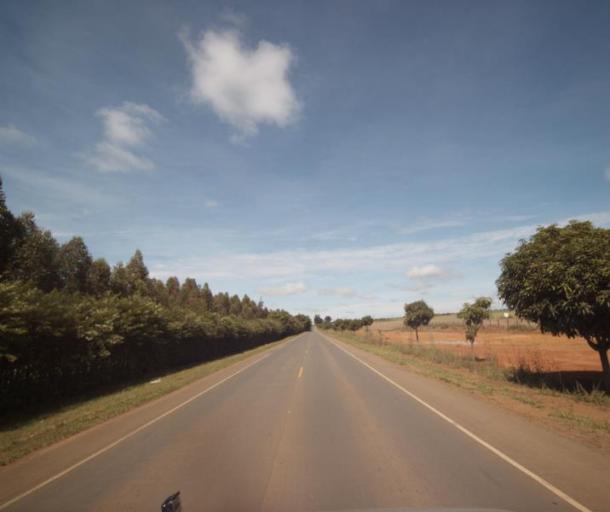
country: BR
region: Goias
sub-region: Anapolis
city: Anapolis
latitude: -16.2135
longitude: -48.9181
